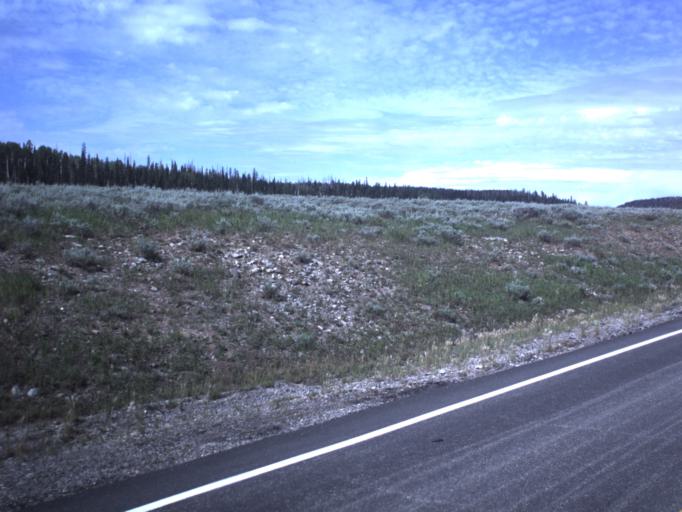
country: US
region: Utah
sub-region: Iron County
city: Parowan
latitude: 37.5693
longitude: -112.7961
